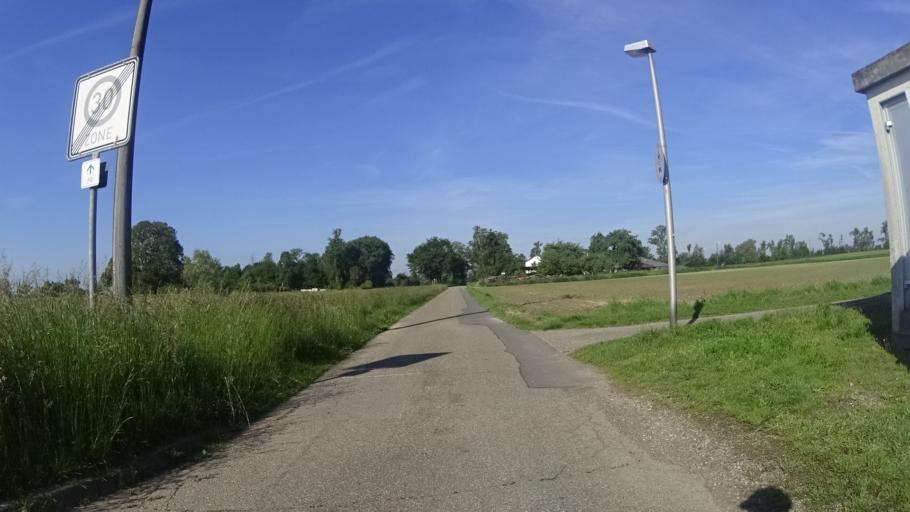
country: DE
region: Baden-Wuerttemberg
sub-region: Freiburg Region
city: Kehl
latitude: 48.5865
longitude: 7.8670
